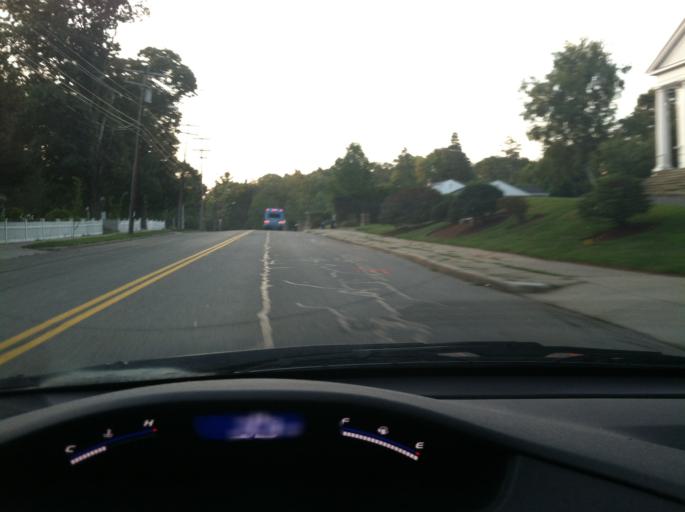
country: US
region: Massachusetts
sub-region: Middlesex County
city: Lexington
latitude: 42.4509
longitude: -71.2310
